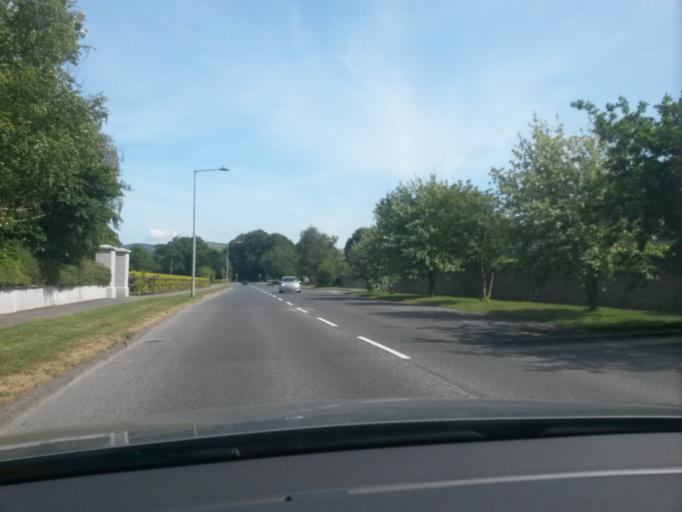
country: IE
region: Leinster
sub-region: Wicklow
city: Blessington
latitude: 53.1701
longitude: -6.5414
